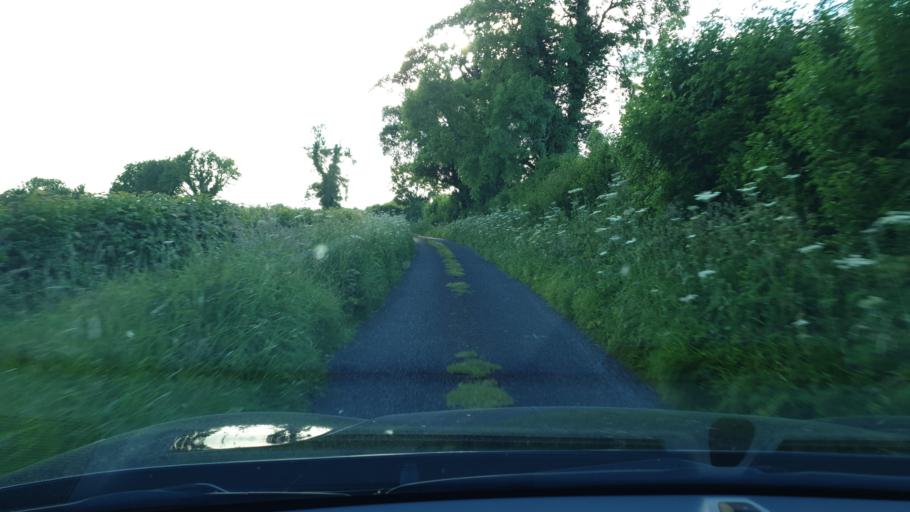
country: IE
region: Leinster
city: Hartstown
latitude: 53.4472
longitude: -6.4022
